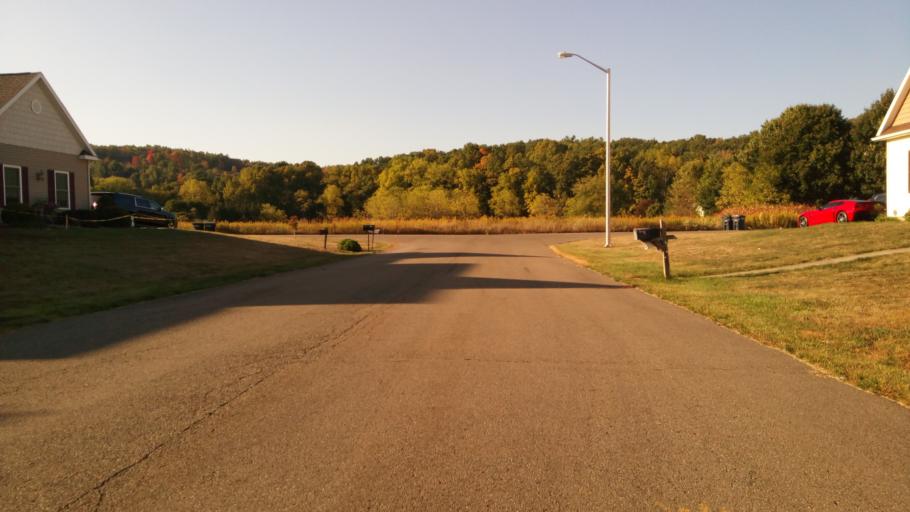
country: US
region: New York
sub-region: Chemung County
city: Southport
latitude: 42.0550
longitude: -76.8332
